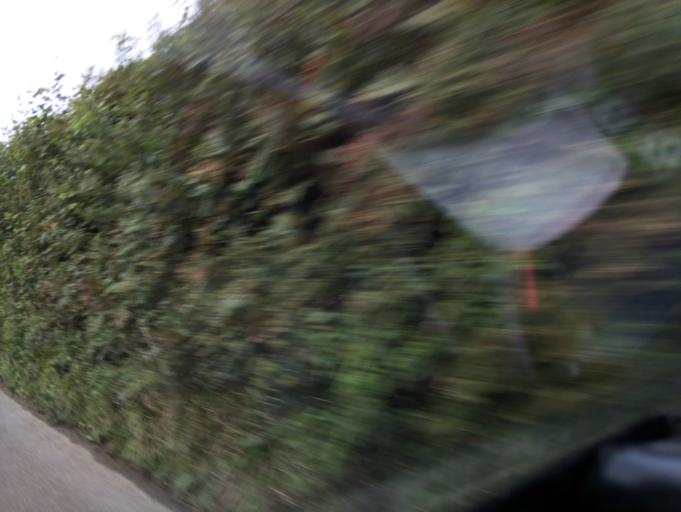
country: GB
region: England
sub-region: Devon
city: Kingsbridge
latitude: 50.2931
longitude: -3.7866
